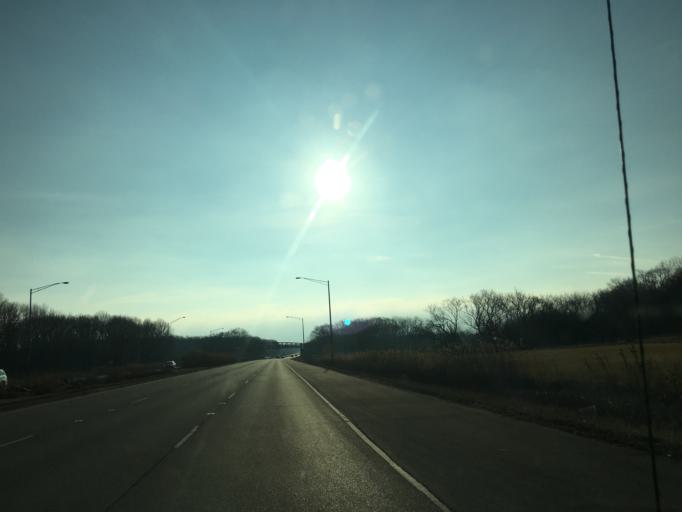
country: US
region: Illinois
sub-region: Cook County
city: Rolling Meadows
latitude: 42.0364
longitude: -88.0293
